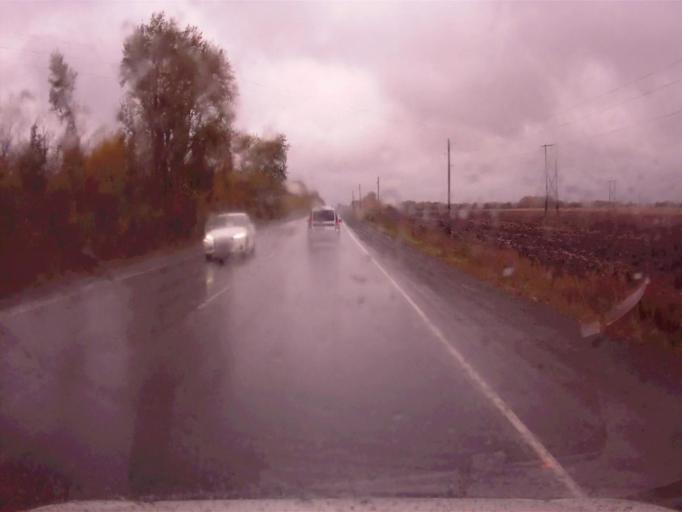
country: RU
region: Chelyabinsk
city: Argayash
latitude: 55.4312
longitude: 60.9888
